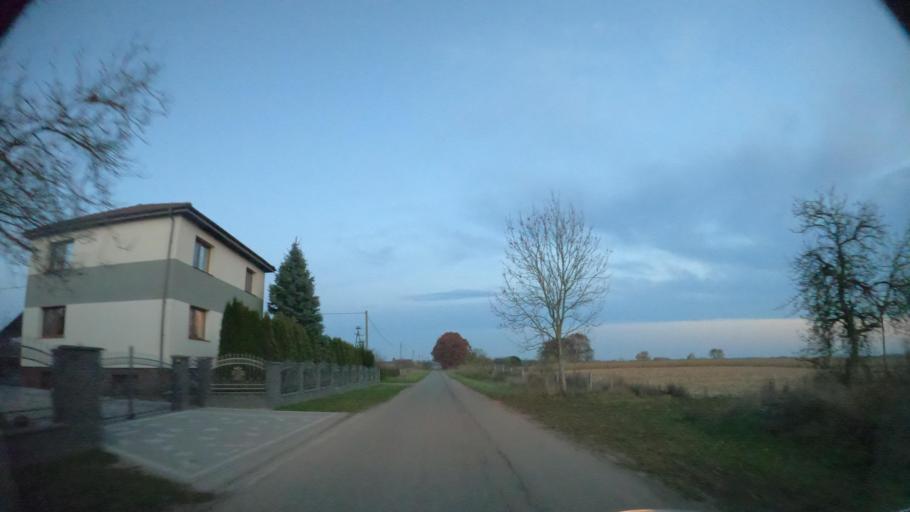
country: PL
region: Greater Poland Voivodeship
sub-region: Powiat zlotowski
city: Sypniewo
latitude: 53.4262
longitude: 16.6218
